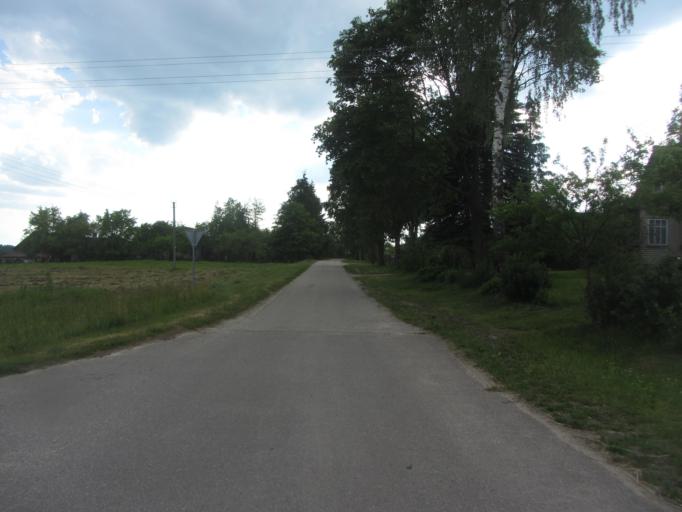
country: LT
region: Alytaus apskritis
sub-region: Alytaus rajonas
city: Daugai
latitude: 54.4696
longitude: 24.2657
